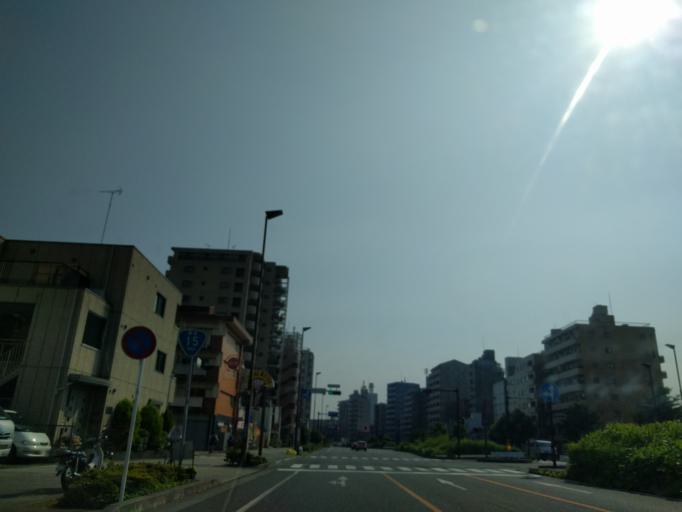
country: JP
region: Kanagawa
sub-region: Kawasaki-shi
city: Kawasaki
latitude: 35.5214
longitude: 139.6928
